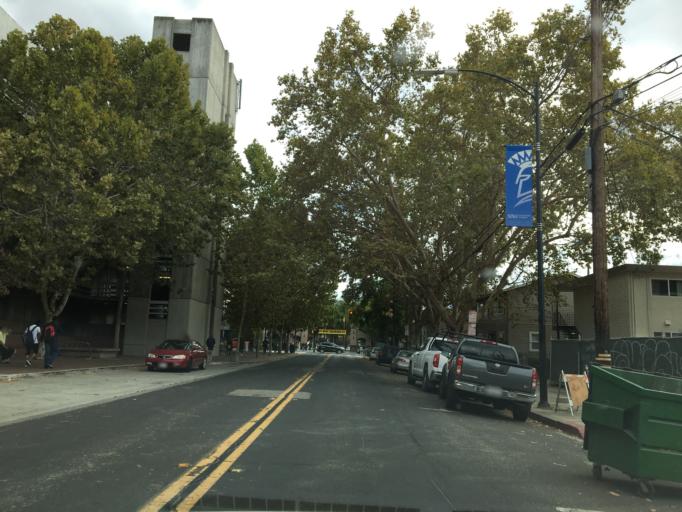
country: US
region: California
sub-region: Santa Clara County
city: San Jose
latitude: 37.3392
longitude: -121.8814
